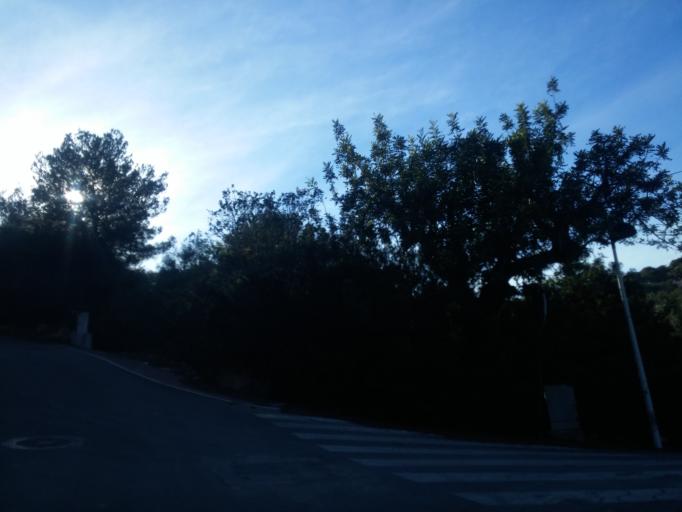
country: ES
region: Valencia
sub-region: Provincia de Alicante
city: Moraira
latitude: 38.6986
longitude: 0.1437
